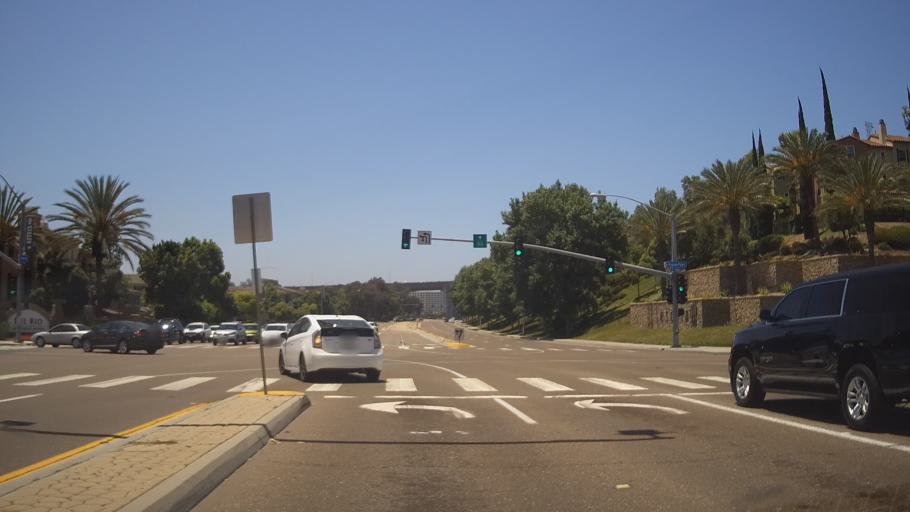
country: US
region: California
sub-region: San Diego County
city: San Diego
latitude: 32.7816
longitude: -117.1318
